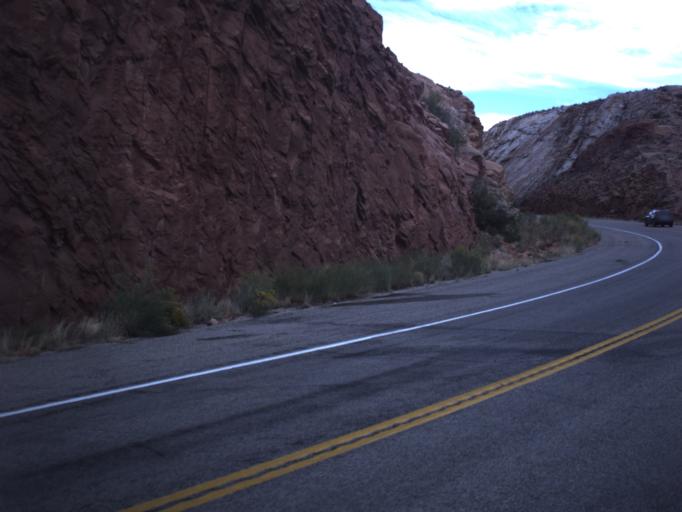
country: US
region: Utah
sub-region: San Juan County
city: Blanding
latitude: 37.2601
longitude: -109.6736
